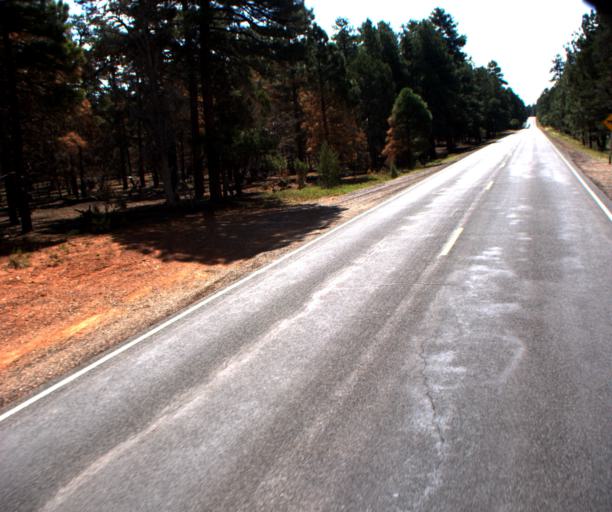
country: US
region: Arizona
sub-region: Coconino County
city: Grand Canyon
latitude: 36.0423
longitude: -112.0800
